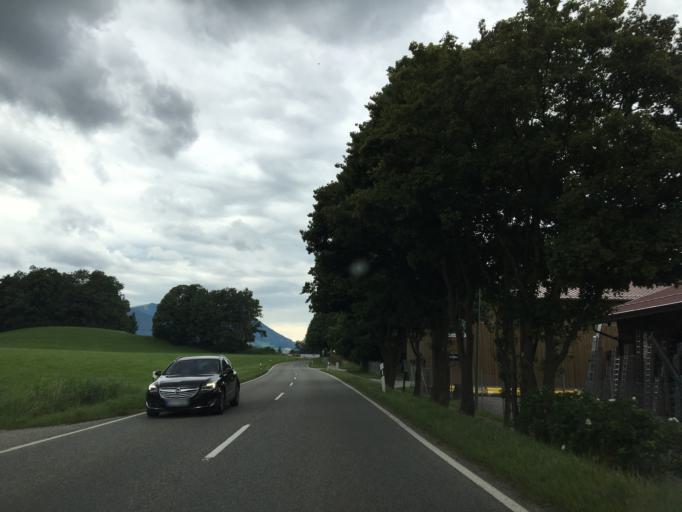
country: DE
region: Bavaria
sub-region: Upper Bavaria
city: Flintsbach
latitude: 47.7161
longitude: 12.1372
